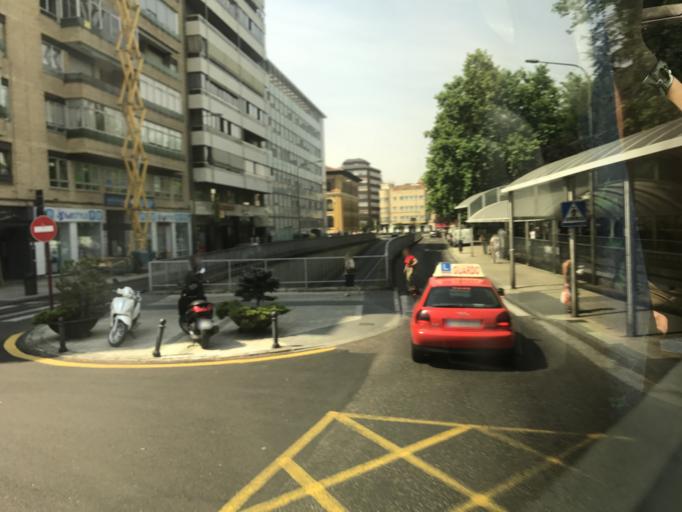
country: ES
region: Castille and Leon
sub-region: Provincia de Palencia
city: Palencia
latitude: 42.0151
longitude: -4.5332
